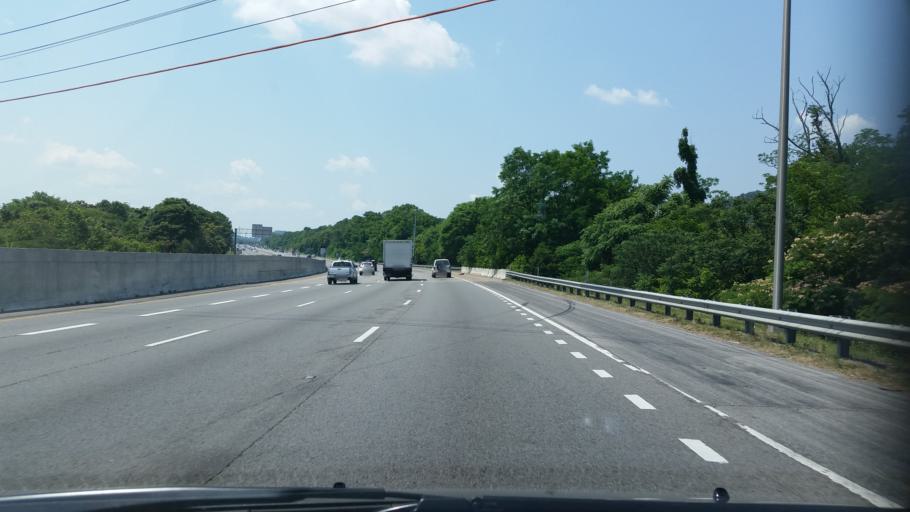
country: US
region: Tennessee
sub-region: Davidson County
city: Oak Hill
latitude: 36.0754
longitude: -86.7684
